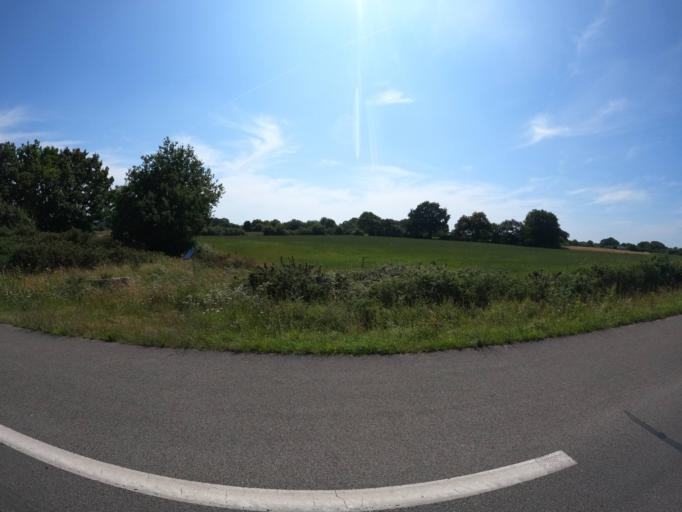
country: FR
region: Pays de la Loire
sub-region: Departement de la Loire-Atlantique
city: Pornic
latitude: 47.1311
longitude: -2.1201
